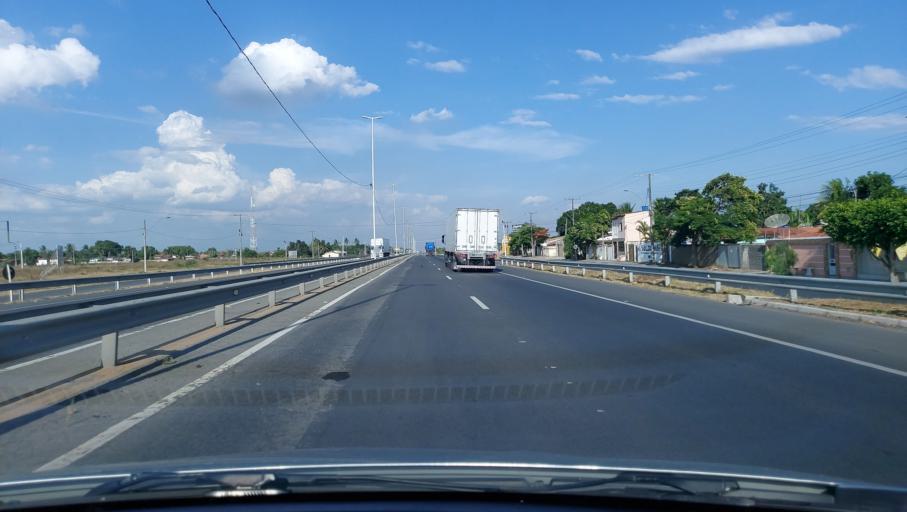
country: BR
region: Bahia
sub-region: Santo Estevao
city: Santo Estevao
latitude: -12.4449
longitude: -39.2392
